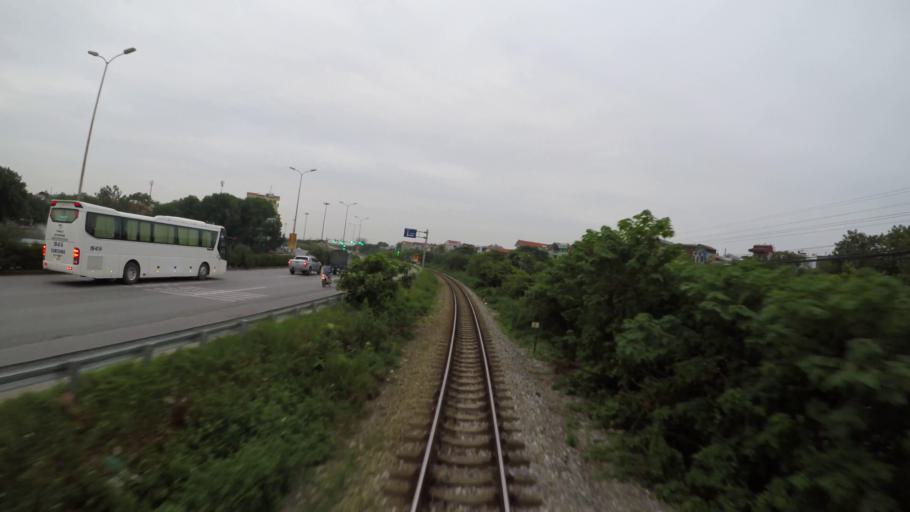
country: VN
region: Ha Noi
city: Trau Quy
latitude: 21.0087
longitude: 105.9552
